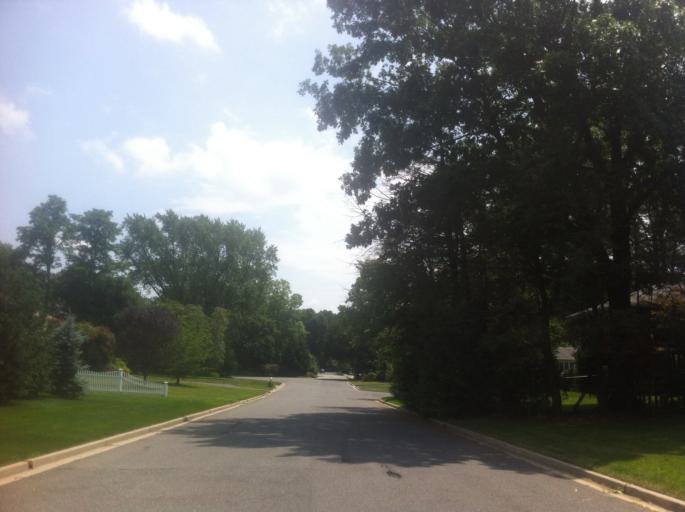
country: US
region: New York
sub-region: Nassau County
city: Locust Valley
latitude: 40.8557
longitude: -73.5965
